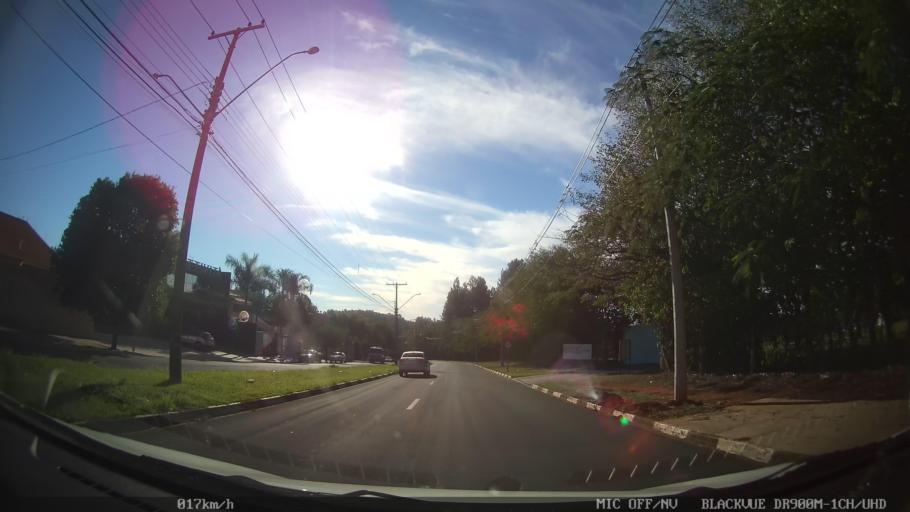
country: BR
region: Sao Paulo
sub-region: Araraquara
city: Araraquara
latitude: -21.7599
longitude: -48.1767
